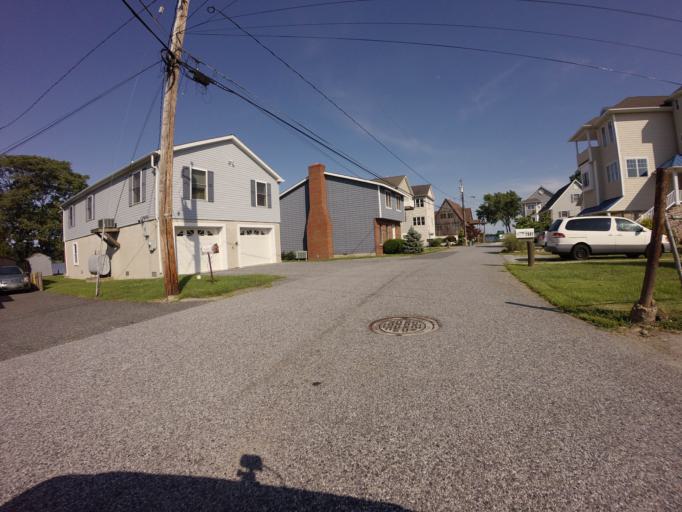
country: US
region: Maryland
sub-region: Baltimore County
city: Edgemere
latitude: 39.2093
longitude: -76.4382
